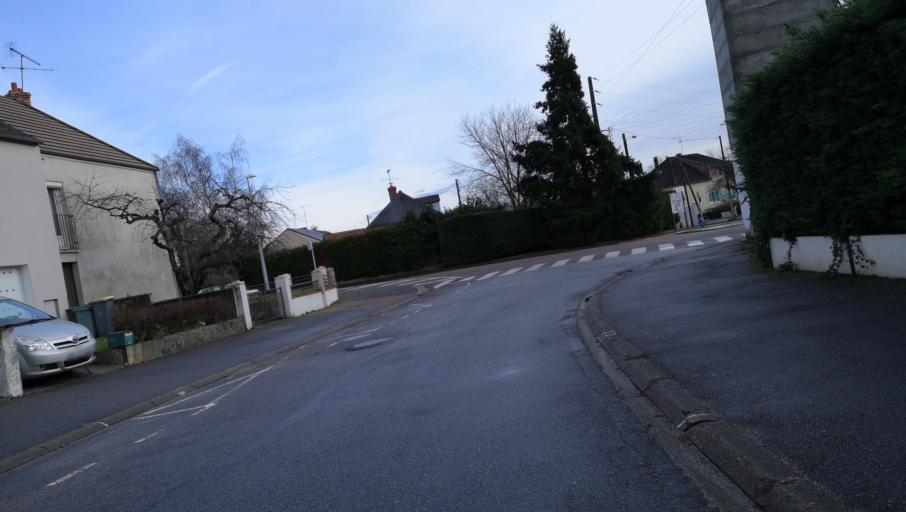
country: FR
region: Centre
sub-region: Departement du Loiret
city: Saint-Jean-de-Braye
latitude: 47.9208
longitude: 1.9644
